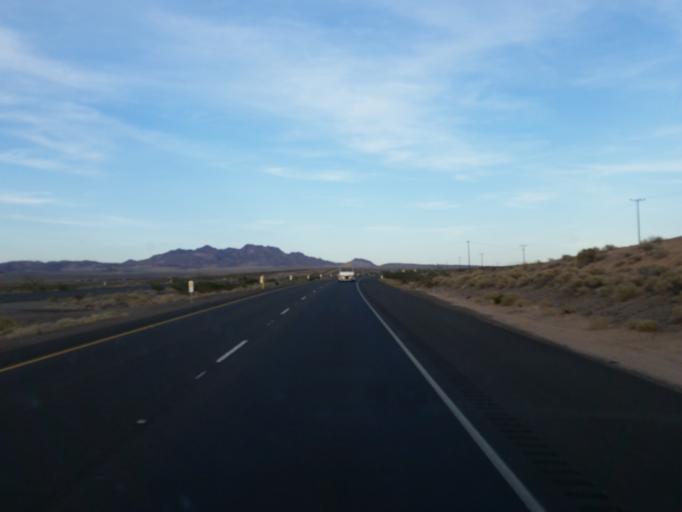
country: US
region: California
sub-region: San Bernardino County
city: Fort Irwin
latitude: 34.7841
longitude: -116.4204
